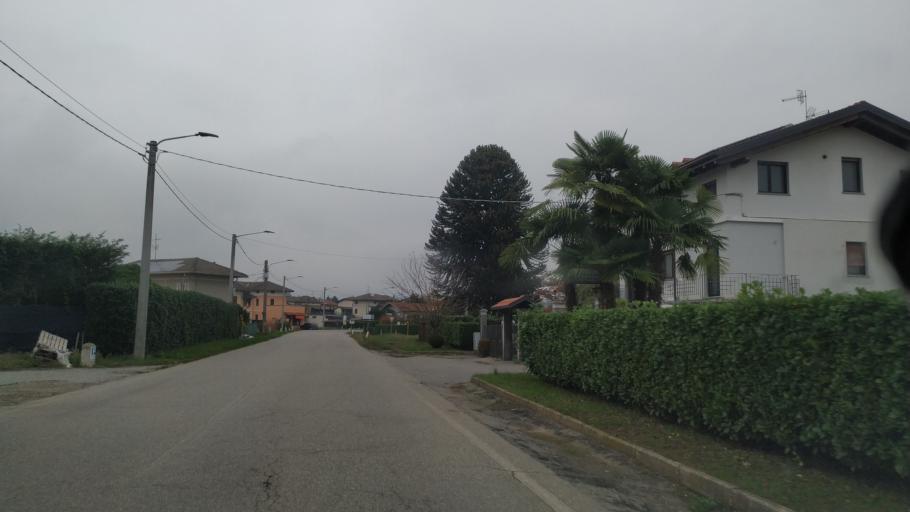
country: IT
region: Piedmont
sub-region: Provincia di Biella
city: Cerreto Castello
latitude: 45.5549
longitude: 8.1718
